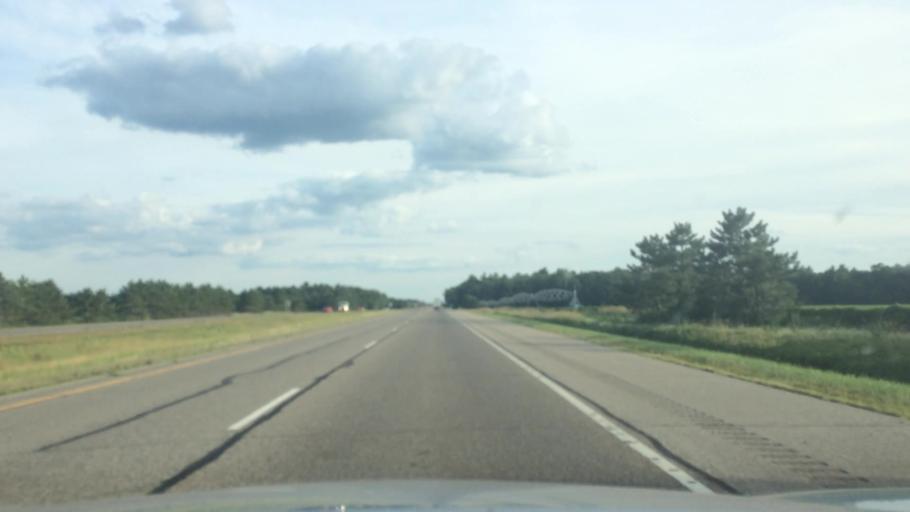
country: US
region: Wisconsin
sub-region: Portage County
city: Plover
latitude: 44.2705
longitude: -89.5239
